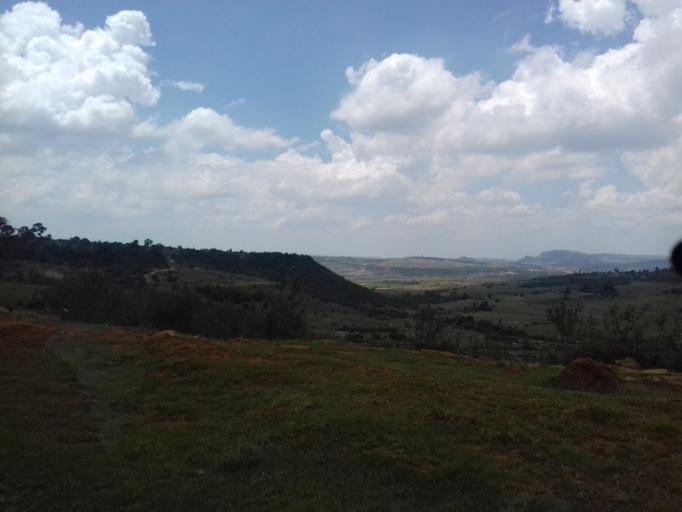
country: LS
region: Maseru
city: Maseru
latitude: -29.4572
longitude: 27.5645
